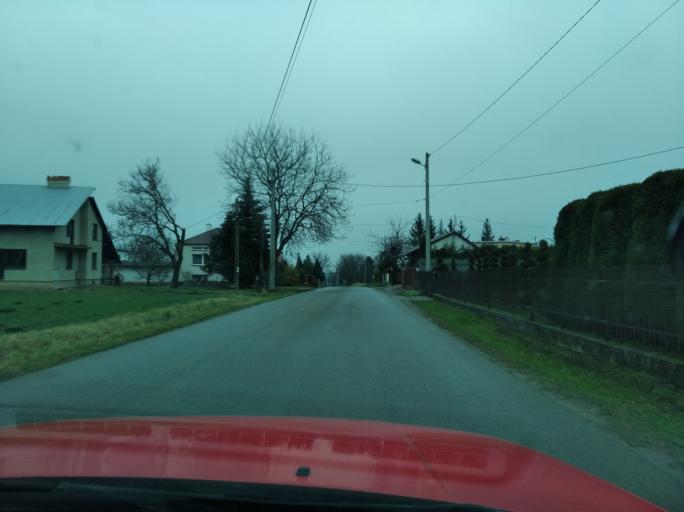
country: PL
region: Subcarpathian Voivodeship
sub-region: Powiat jaroslawski
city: Wierzbna
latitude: 50.0293
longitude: 22.6038
